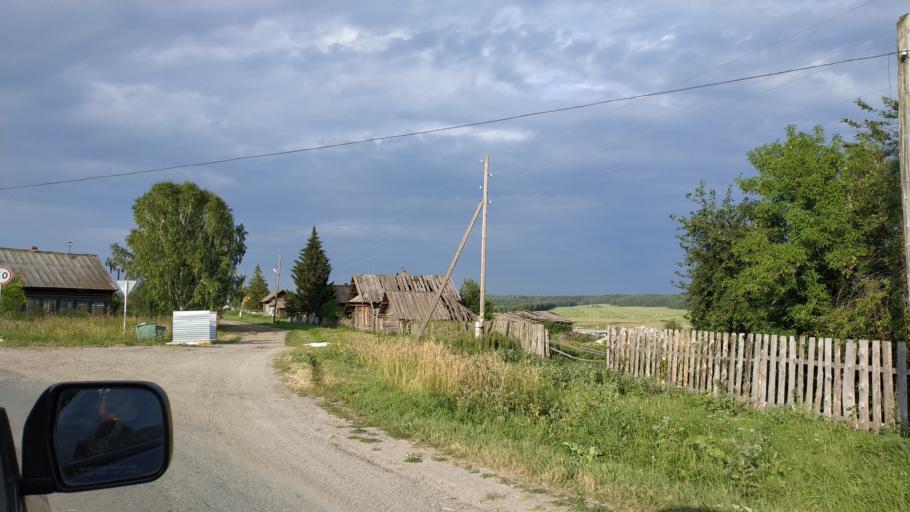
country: RU
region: Sverdlovsk
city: Yelanskiy
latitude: 57.0823
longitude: 62.4747
